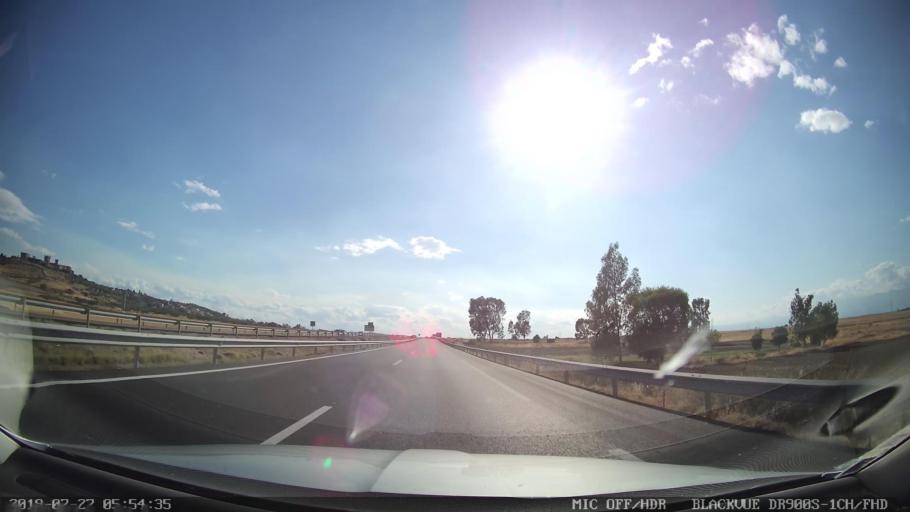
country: ES
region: Castille-La Mancha
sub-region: Province of Toledo
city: Oropesa
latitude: 39.9275
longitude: -5.1712
